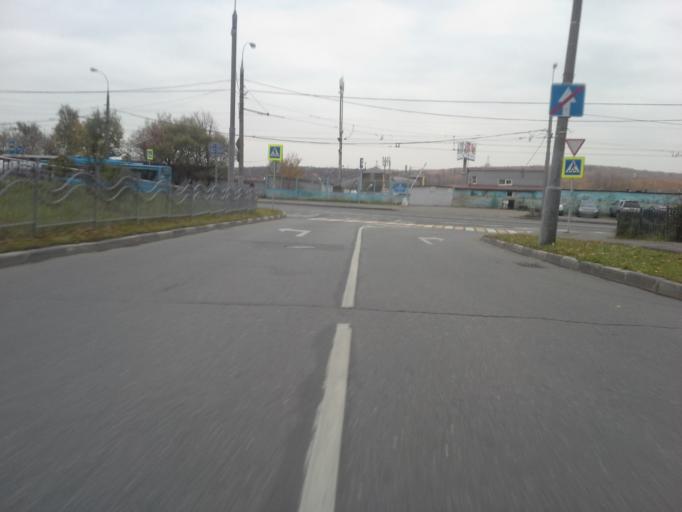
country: RU
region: Moscow
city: Yasenevo
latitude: 55.5895
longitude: 37.5454
